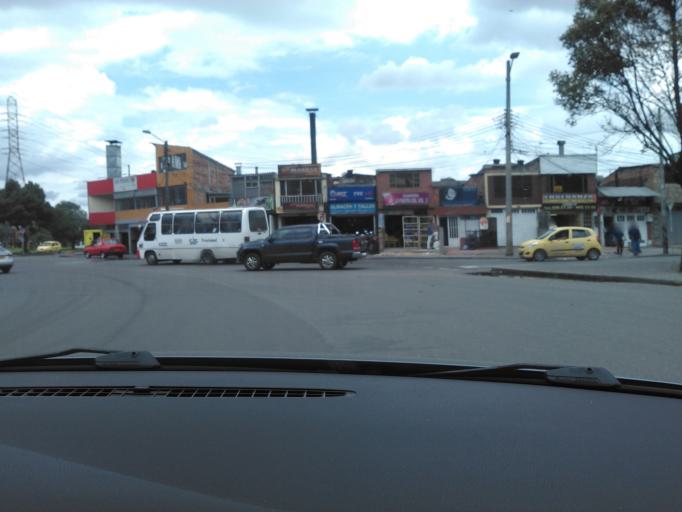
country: CO
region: Bogota D.C.
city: Bogota
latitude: 4.6155
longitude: -74.1148
